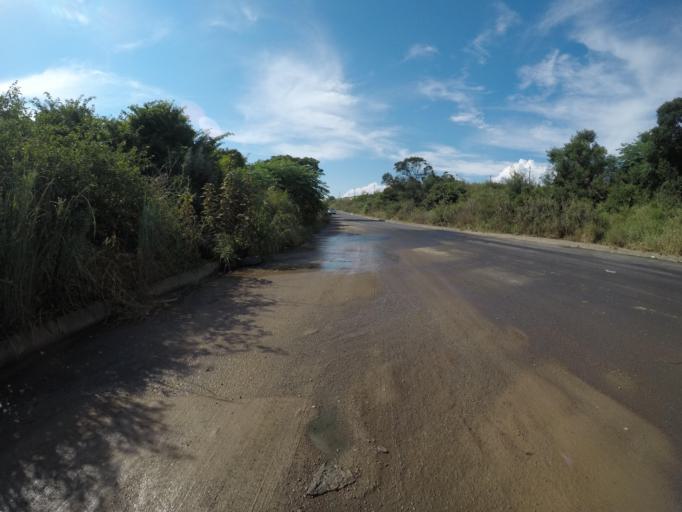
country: ZA
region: Eastern Cape
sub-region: Buffalo City Metropolitan Municipality
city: East London
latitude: -33.0096
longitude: 27.8582
